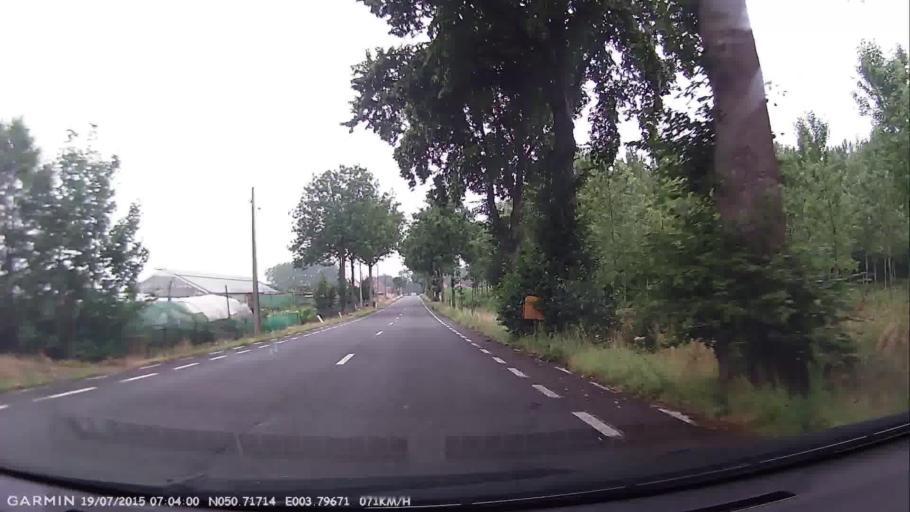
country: BE
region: Wallonia
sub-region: Province du Hainaut
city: Lessines
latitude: 50.7172
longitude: 3.7964
